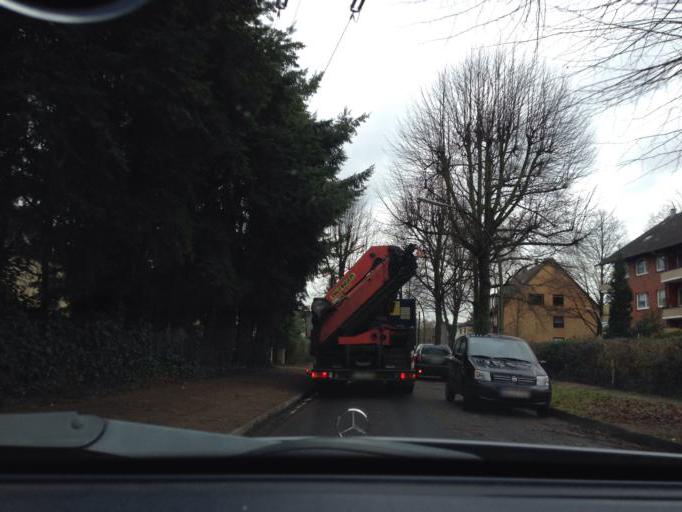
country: DE
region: Hamburg
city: Farmsen-Berne
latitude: 53.5851
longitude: 10.1149
